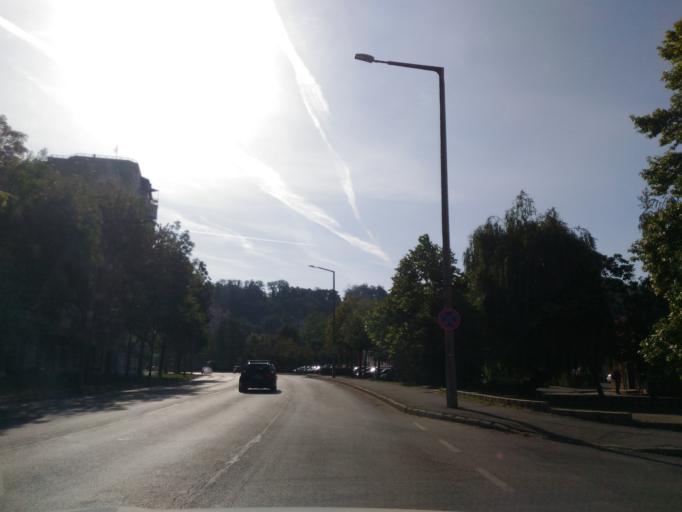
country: HU
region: Baranya
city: Komlo
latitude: 46.1898
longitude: 18.2661
